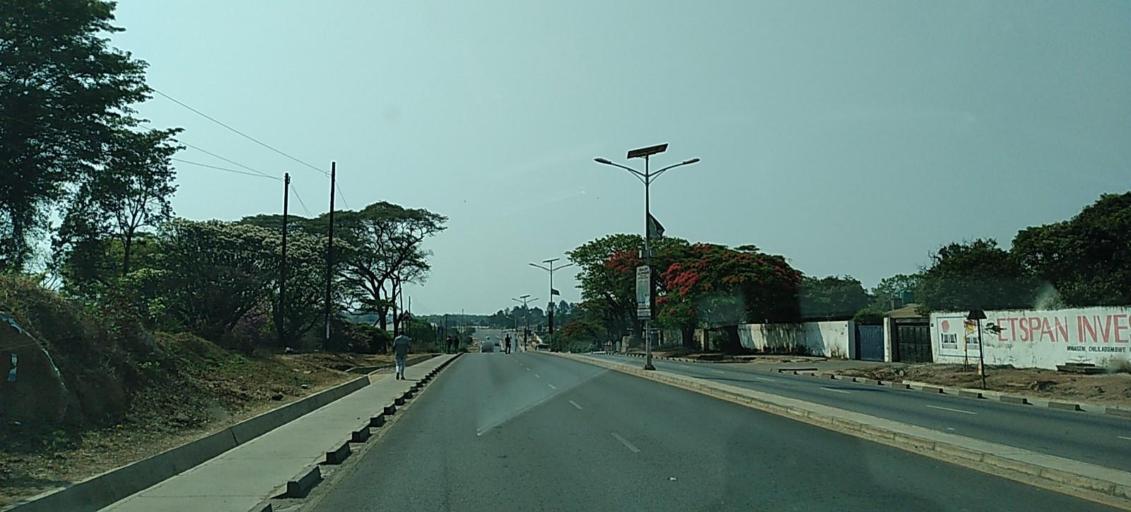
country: ZM
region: Copperbelt
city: Chingola
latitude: -12.5533
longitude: 27.8700
